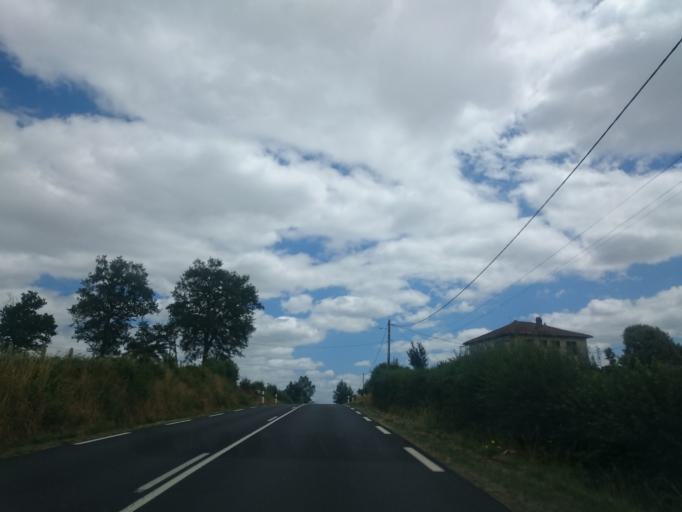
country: FR
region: Auvergne
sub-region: Departement du Cantal
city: Saint-Paul-des-Landes
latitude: 44.9524
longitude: 2.2879
